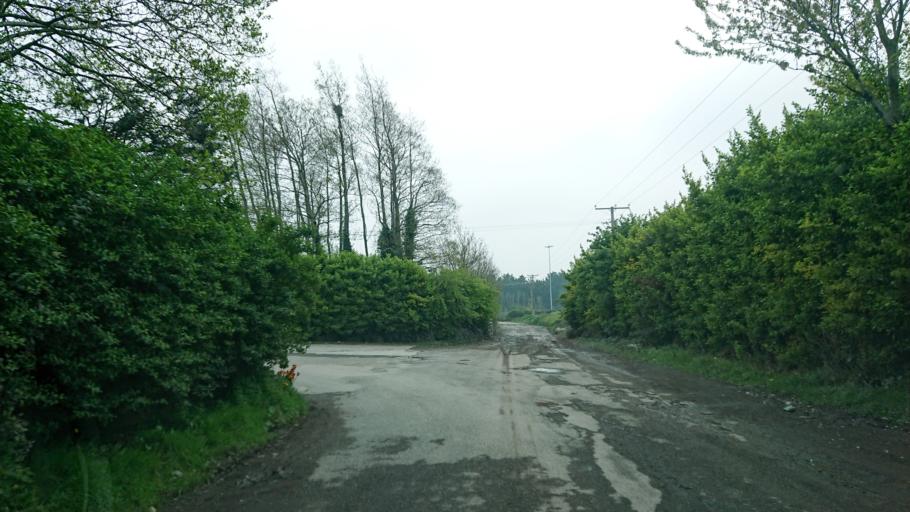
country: IE
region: Leinster
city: Ballymun
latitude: 53.4110
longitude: -6.2612
